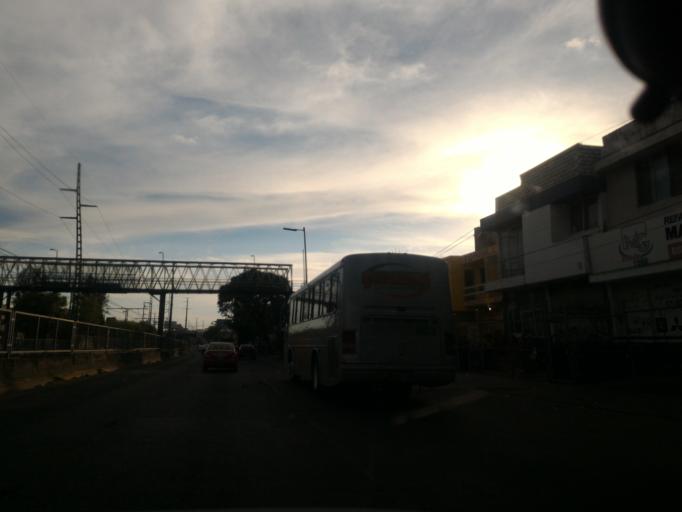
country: MX
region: Jalisco
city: Guadalajara
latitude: 20.6359
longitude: -103.3785
